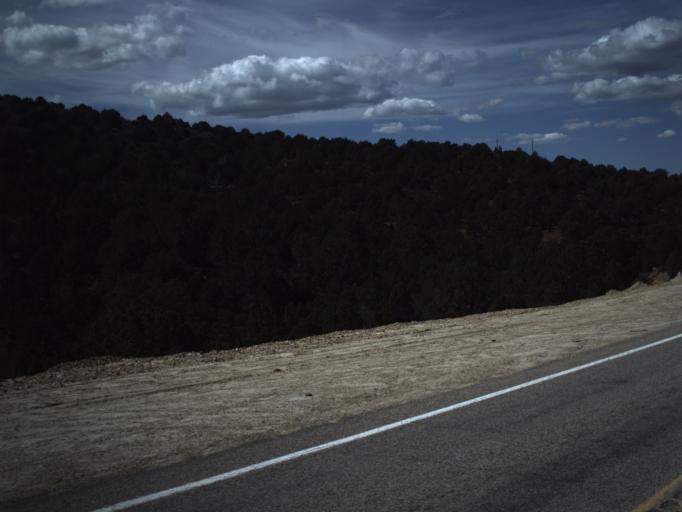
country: US
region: Utah
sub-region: Washington County
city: Enterprise
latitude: 37.5318
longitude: -113.6490
